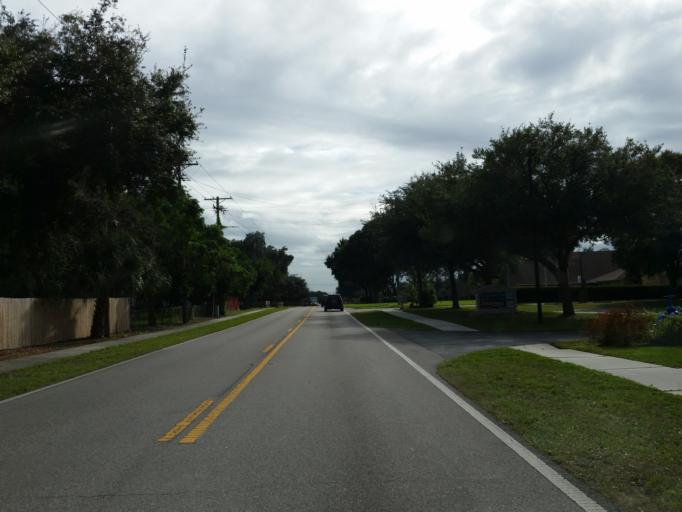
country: US
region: Florida
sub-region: Hillsborough County
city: Brandon
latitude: 27.9199
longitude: -82.2857
